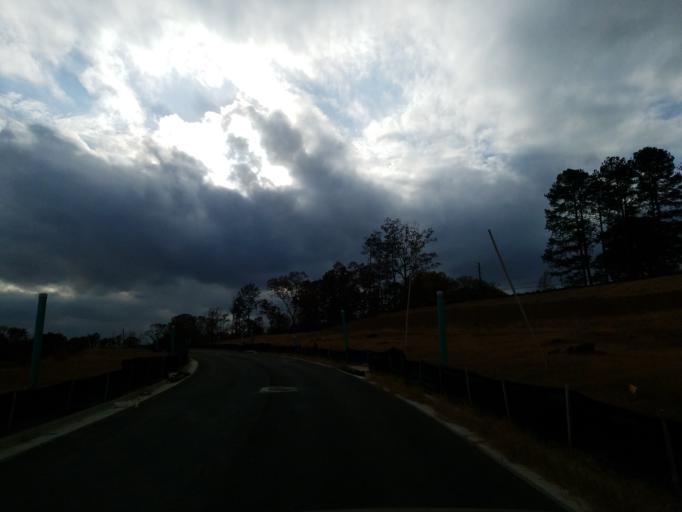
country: US
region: Georgia
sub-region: Cobb County
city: Fair Oaks
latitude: 33.8939
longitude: -84.5437
